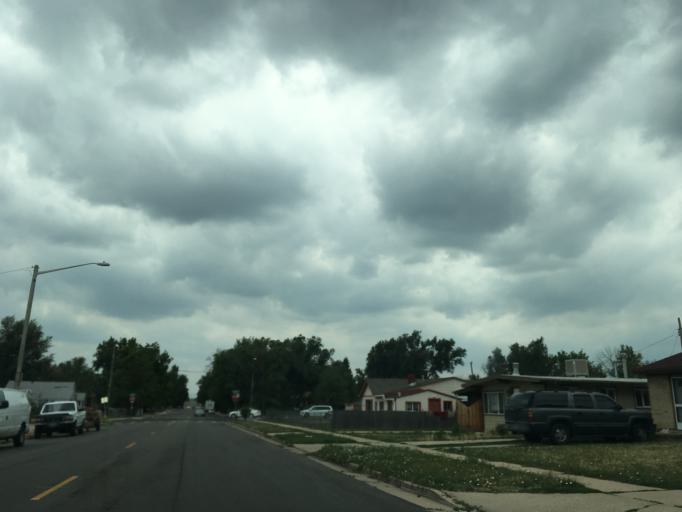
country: US
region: Colorado
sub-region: Arapahoe County
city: Sheridan
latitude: 39.6833
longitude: -105.0159
